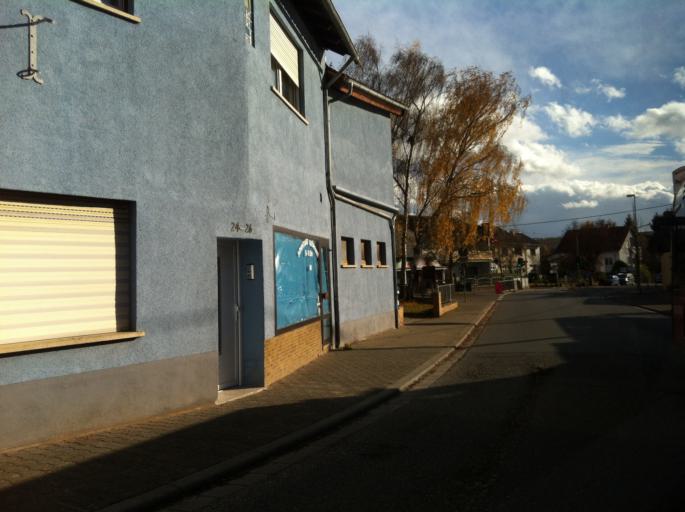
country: DE
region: Rheinland-Pfalz
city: Stadecken-Elsheim
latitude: 49.9148
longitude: 8.1238
